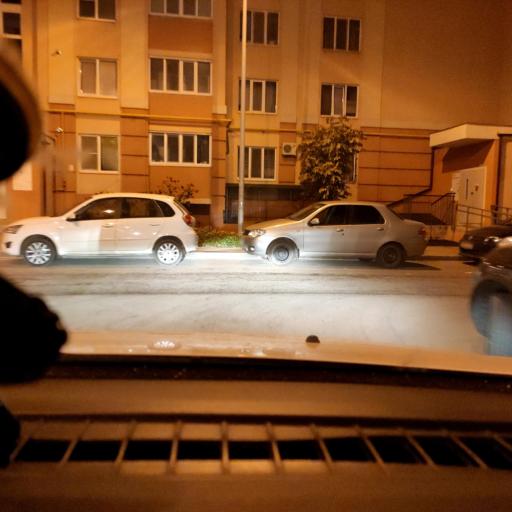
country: RU
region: Samara
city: Samara
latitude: 53.1183
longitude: 50.1562
